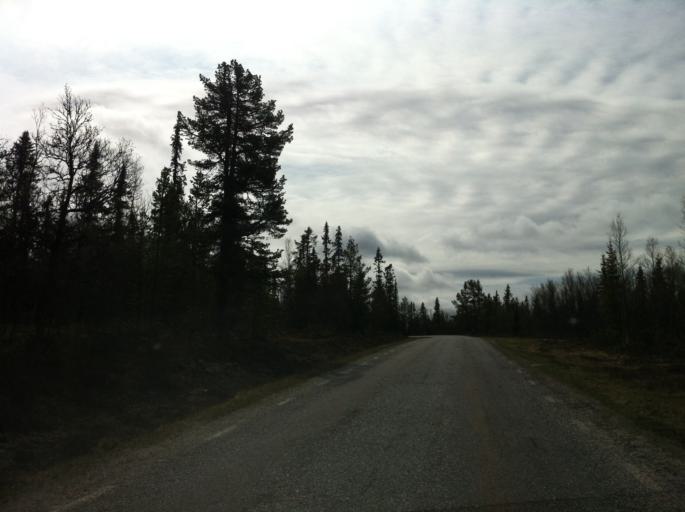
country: NO
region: Hedmark
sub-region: Engerdal
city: Engerdal
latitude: 62.3099
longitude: 12.8088
